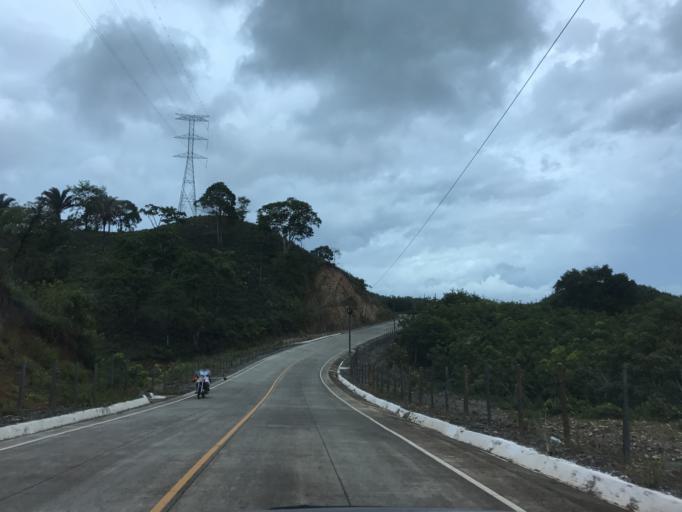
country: GT
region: Izabal
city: Morales
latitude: 15.6337
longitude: -89.0469
